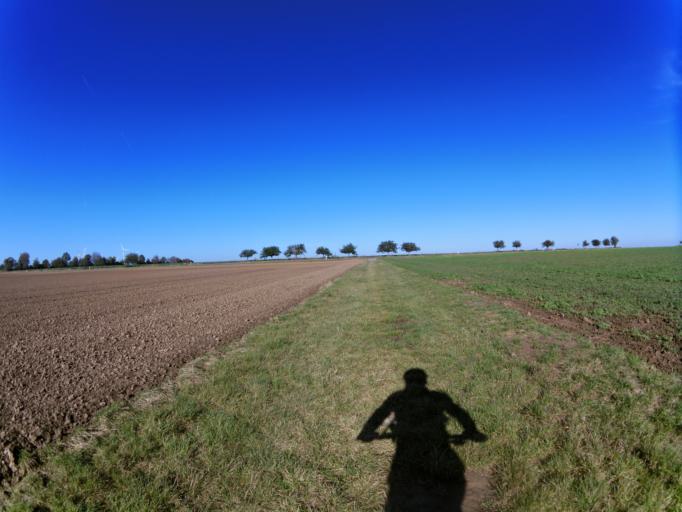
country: DE
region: Bavaria
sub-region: Regierungsbezirk Unterfranken
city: Geroldshausen
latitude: 49.6877
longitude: 9.9169
